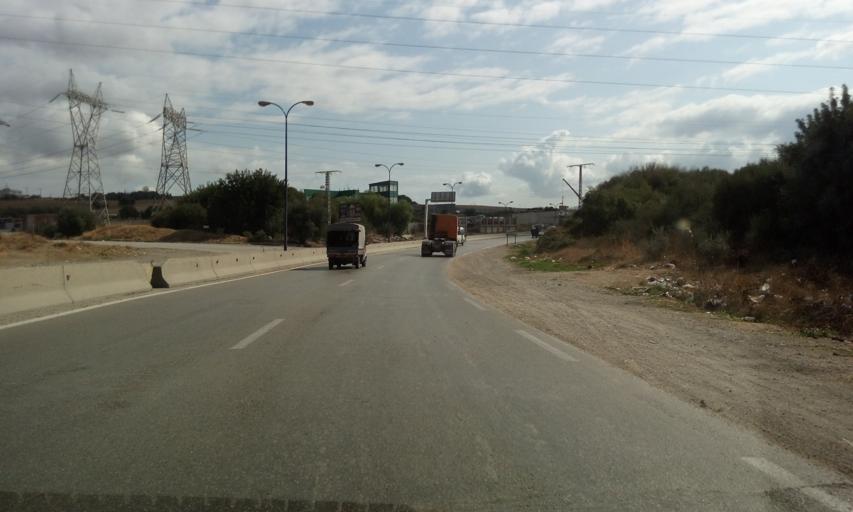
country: DZ
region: Bejaia
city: El Kseur
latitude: 36.6760
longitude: 4.8679
